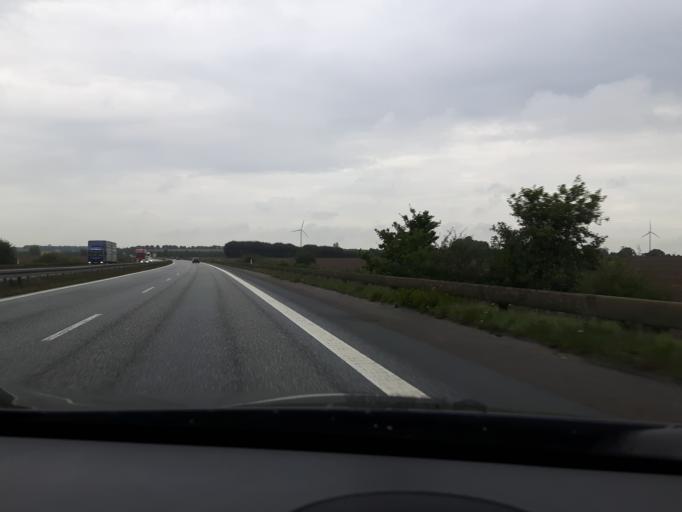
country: DK
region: Central Jutland
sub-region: Randers Kommune
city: Spentrup
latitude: 56.5112
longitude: 9.9692
